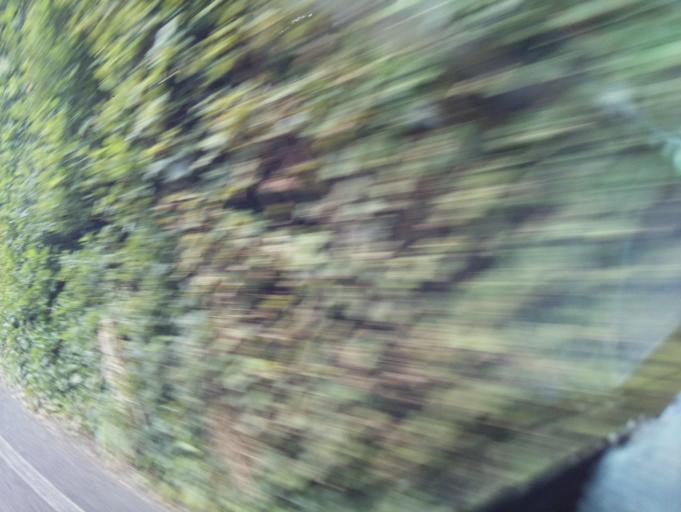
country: GB
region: England
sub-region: North Somerset
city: Nailsea
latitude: 51.4452
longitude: -2.7337
